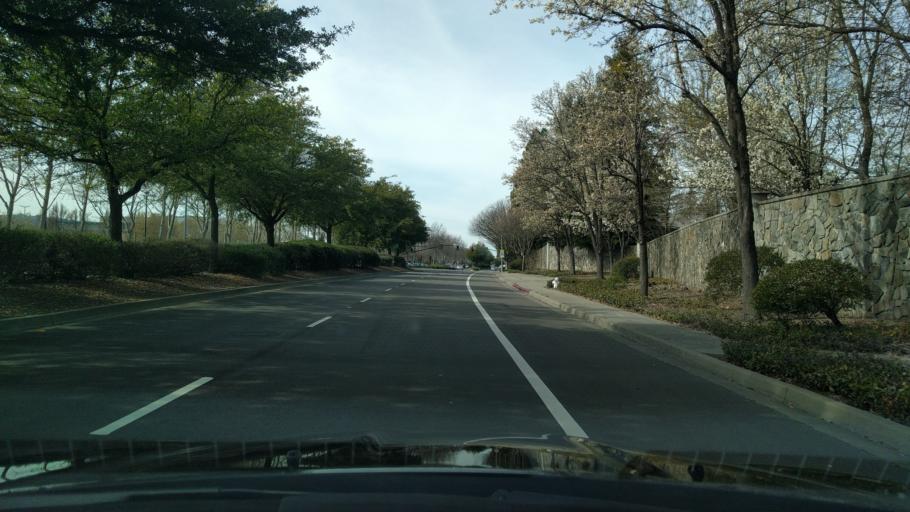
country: US
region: California
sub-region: Contra Costa County
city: San Ramon
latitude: 37.7688
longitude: -121.9551
